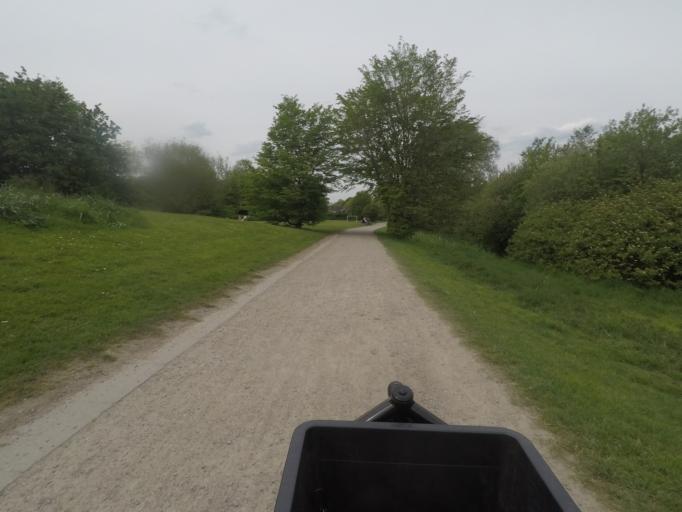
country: DE
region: Hamburg
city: Sasel
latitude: 53.6317
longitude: 10.1194
